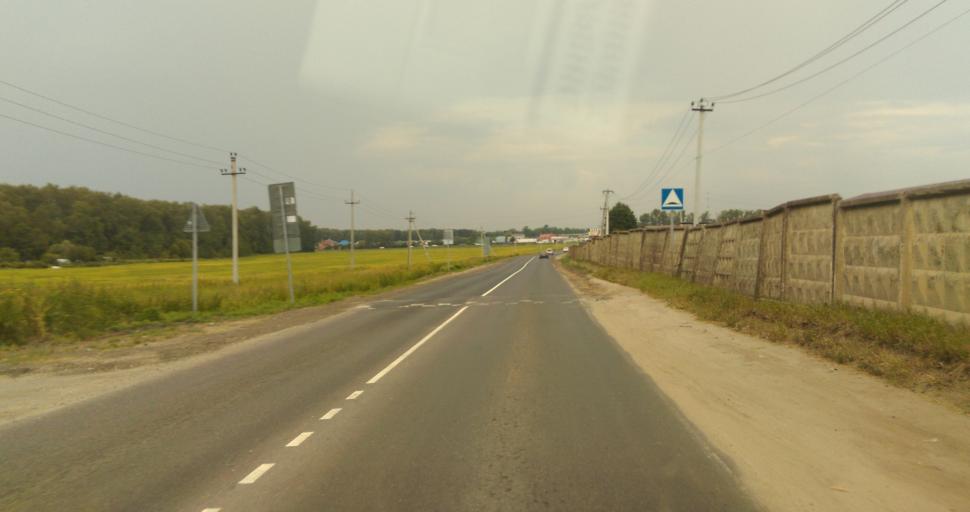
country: RU
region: Moskovskaya
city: Zhitnevo
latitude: 55.3457
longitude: 37.9018
